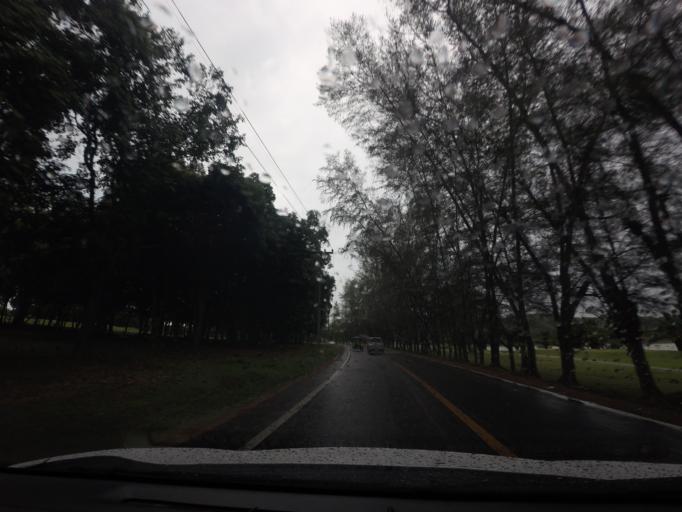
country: TH
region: Chon Buri
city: Sattahip
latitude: 12.7044
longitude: 100.9589
